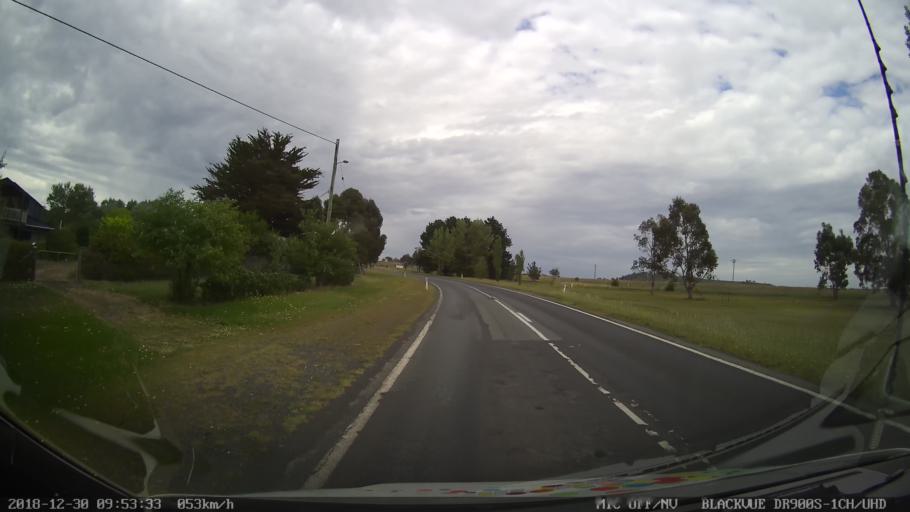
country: AU
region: New South Wales
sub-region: Cooma-Monaro
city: Cooma
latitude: -36.5166
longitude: 149.2817
